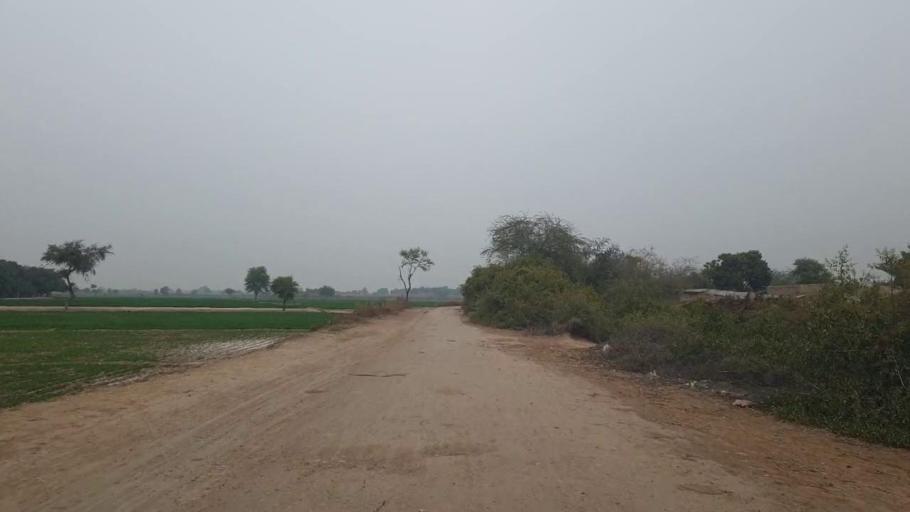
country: PK
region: Sindh
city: Tando Adam
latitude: 25.8353
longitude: 68.6558
